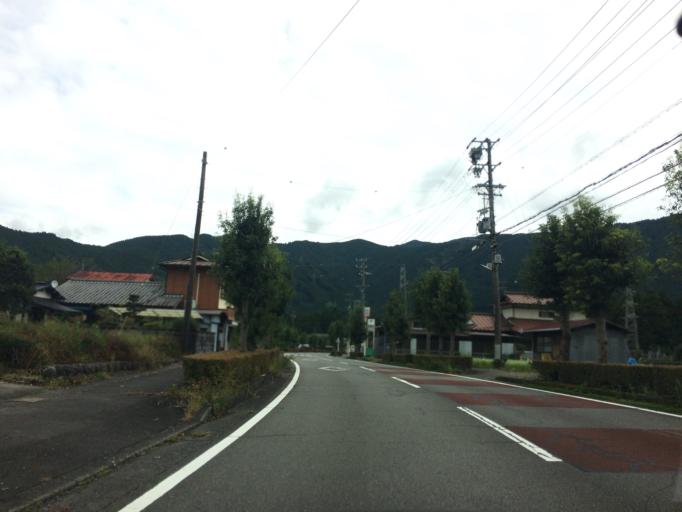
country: JP
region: Shizuoka
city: Kanaya
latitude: 35.0772
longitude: 138.1055
